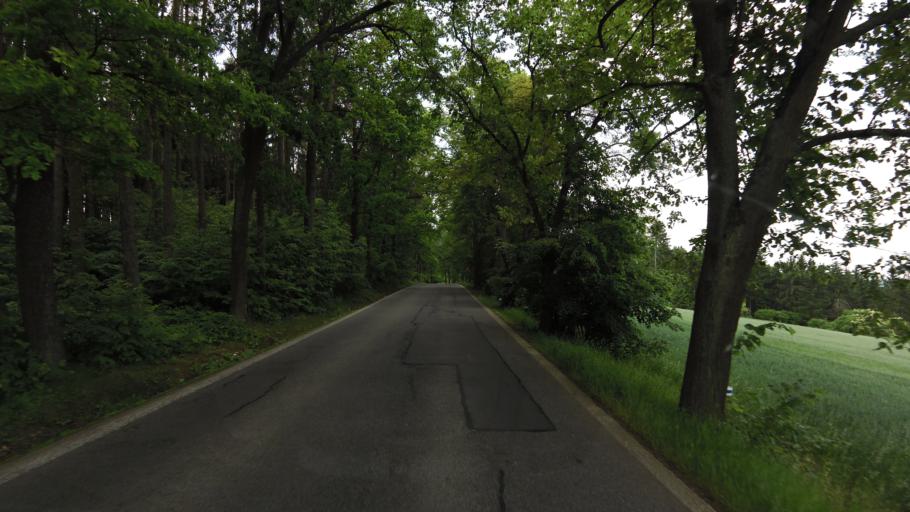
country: CZ
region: Plzensky
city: St'ahlavy
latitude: 49.6942
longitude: 13.5195
